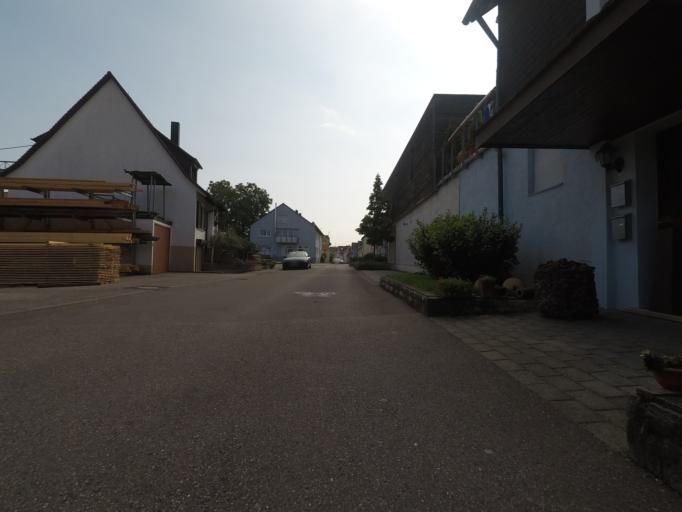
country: DE
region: Baden-Wuerttemberg
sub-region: Regierungsbezirk Stuttgart
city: Winterbach
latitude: 48.7998
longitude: 9.4744
